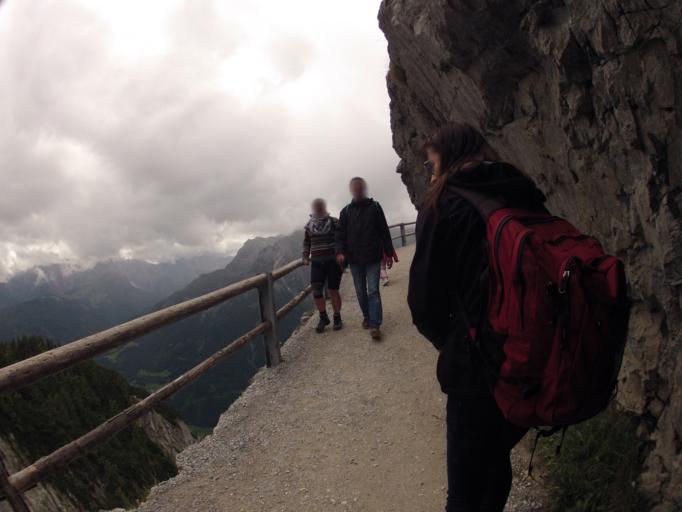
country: AT
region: Salzburg
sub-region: Politischer Bezirk Sankt Johann im Pongau
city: Werfen
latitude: 47.5101
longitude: 13.1934
